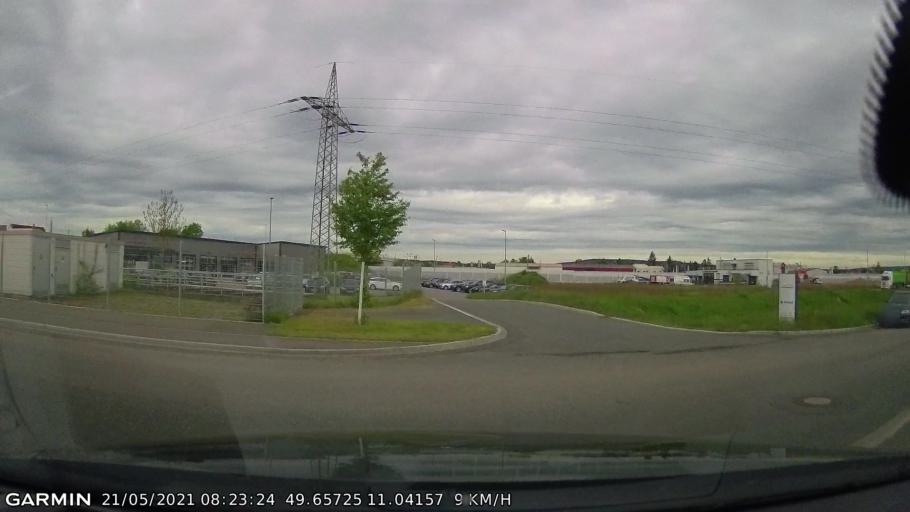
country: DE
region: Bavaria
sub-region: Regierungsbezirk Mittelfranken
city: Baiersdorf
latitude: 49.6576
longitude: 11.0419
